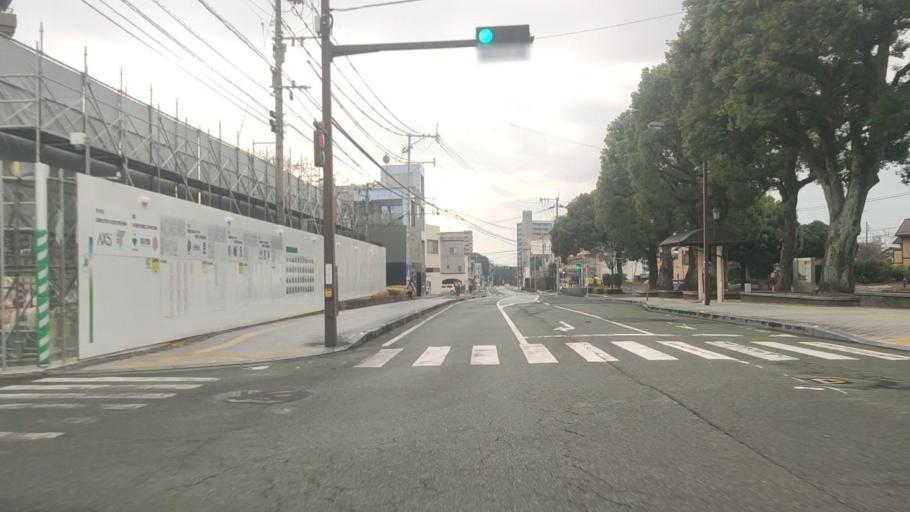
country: JP
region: Kumamoto
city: Kumamoto
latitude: 32.7914
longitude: 130.7404
